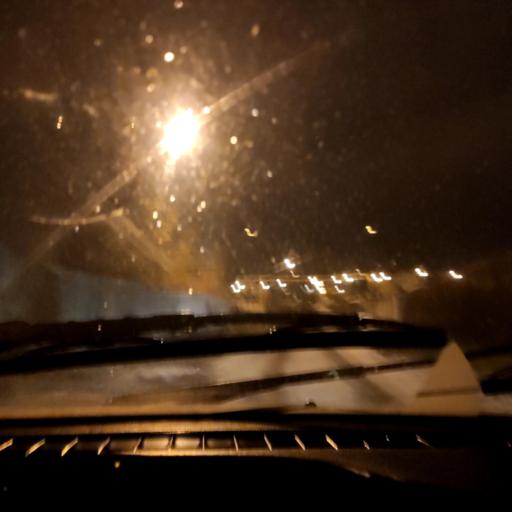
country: RU
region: Samara
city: Zhigulevsk
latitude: 53.4847
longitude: 49.5282
